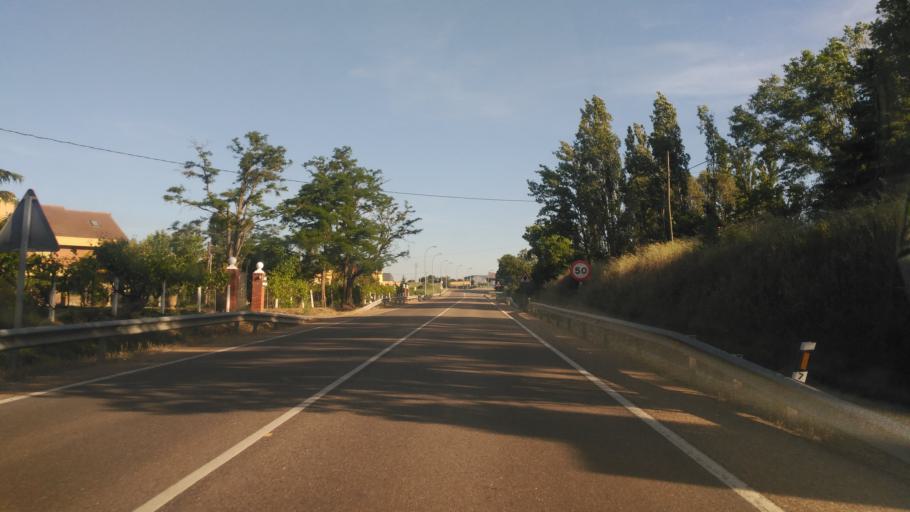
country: ES
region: Castille and Leon
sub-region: Provincia de Zamora
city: Morales del Vino
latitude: 41.4554
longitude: -5.7312
